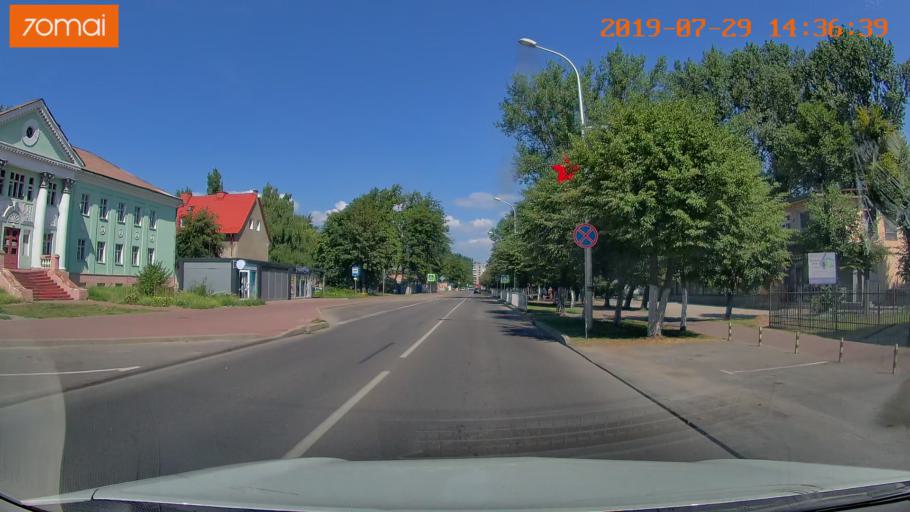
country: RU
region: Kaliningrad
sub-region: Gorod Kaliningrad
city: Baltiysk
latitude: 54.6480
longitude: 19.9017
